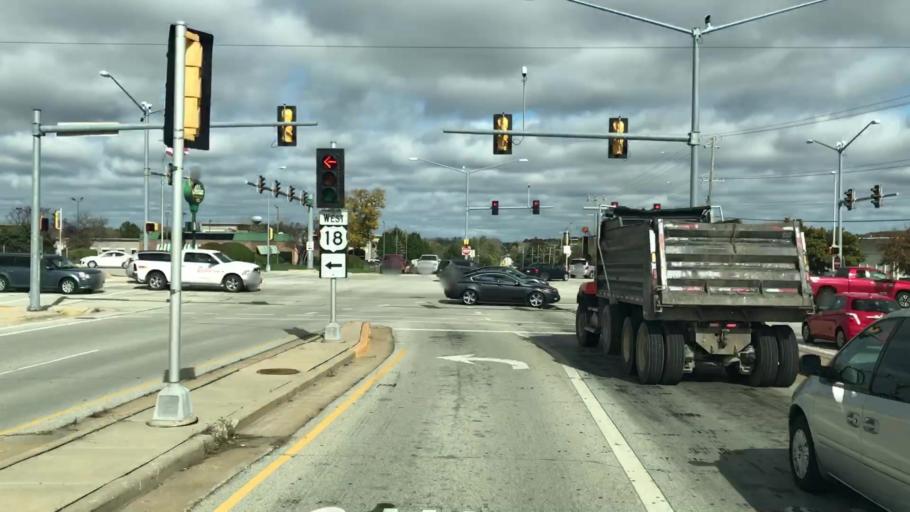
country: US
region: Wisconsin
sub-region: Waukesha County
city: Brookfield
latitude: 43.0357
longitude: -88.1668
